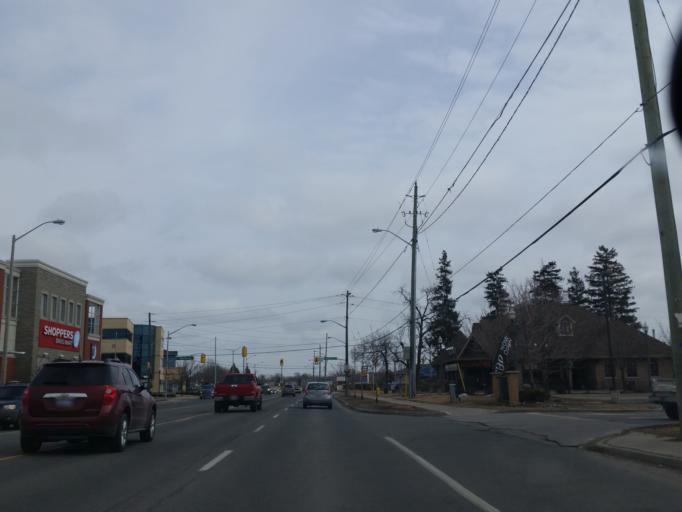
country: CA
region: Ontario
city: Oshawa
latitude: 43.9068
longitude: -78.8095
